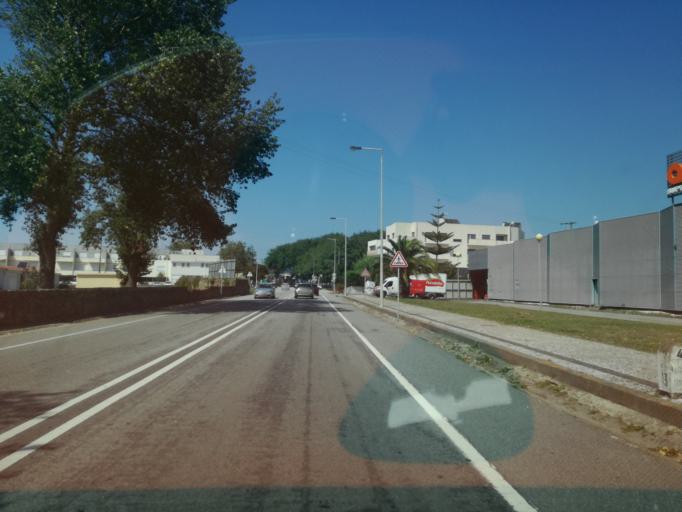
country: PT
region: Braga
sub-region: Esposende
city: Esposende
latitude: 41.5295
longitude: -8.7760
